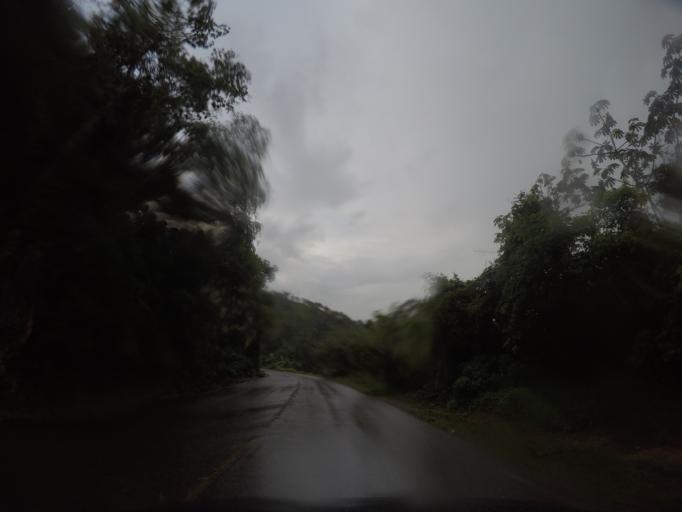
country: MX
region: Oaxaca
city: San Gabriel Mixtepec
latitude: 16.0727
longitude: -97.0793
